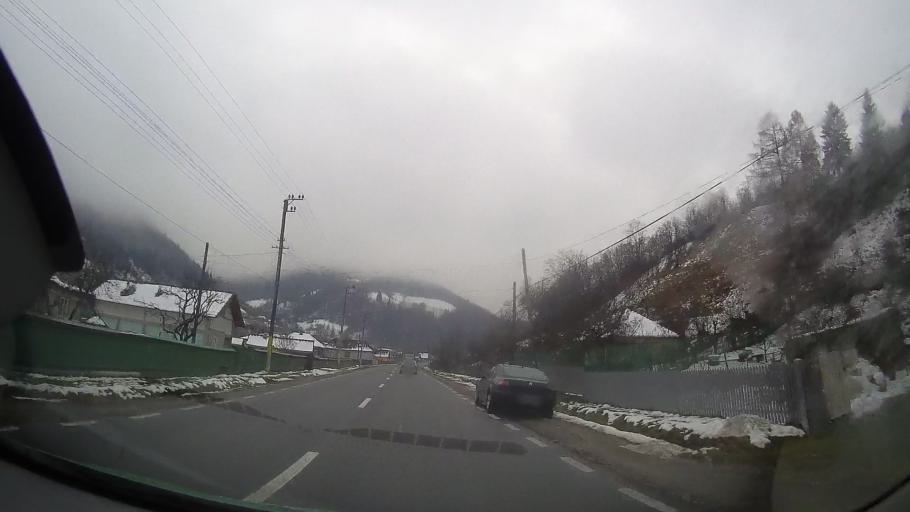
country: RO
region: Neamt
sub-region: Comuna Bicazu Ardelean
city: Bicazu Ardelean
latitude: 46.8566
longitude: 25.9361
